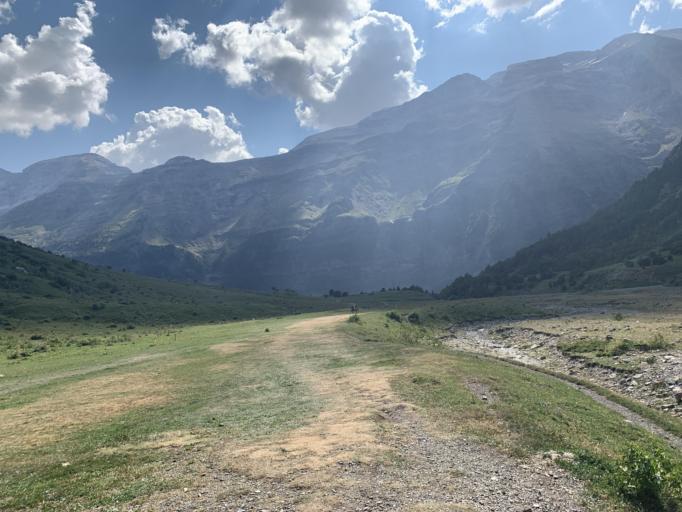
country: ES
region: Aragon
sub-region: Provincia de Huesca
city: Bielsa
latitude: 42.6905
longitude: 0.0876
